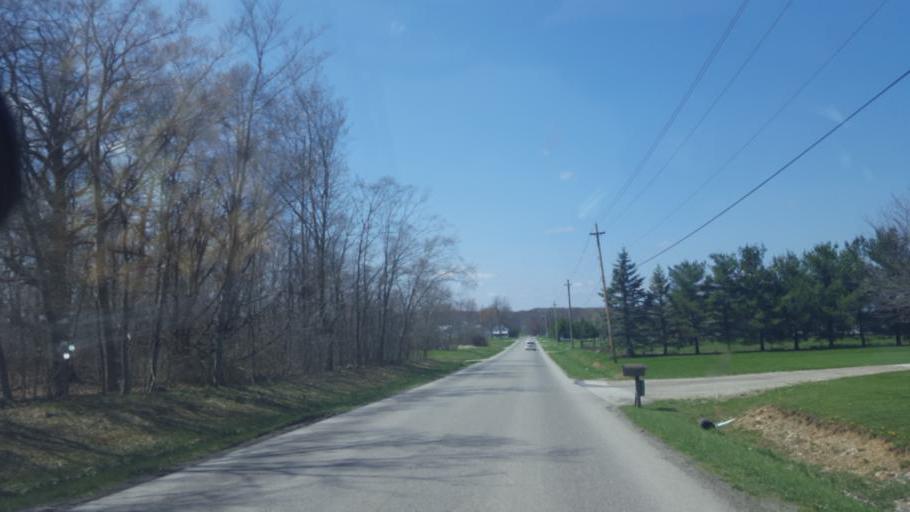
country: US
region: Ohio
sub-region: Geauga County
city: Middlefield
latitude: 41.4260
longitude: -81.1000
